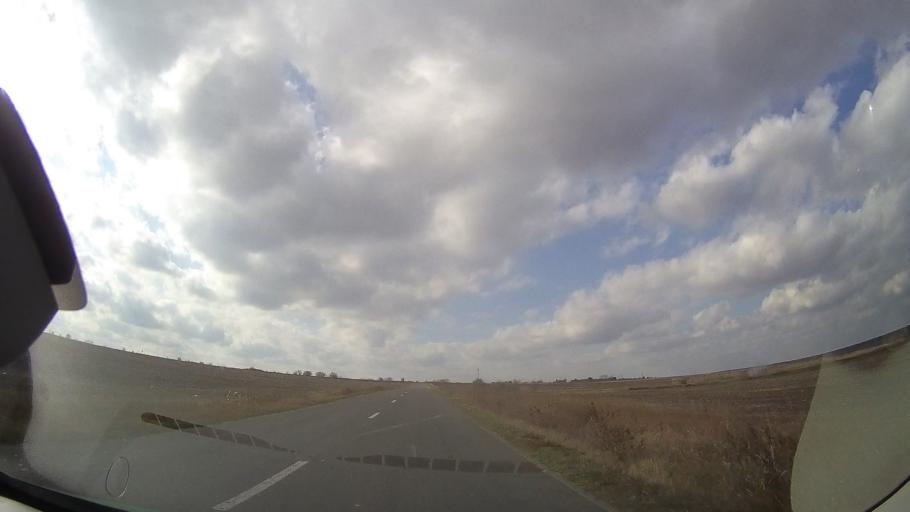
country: RO
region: Constanta
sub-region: Comuna Pecineaga
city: Pecineaga
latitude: 43.8981
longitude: 28.5225
